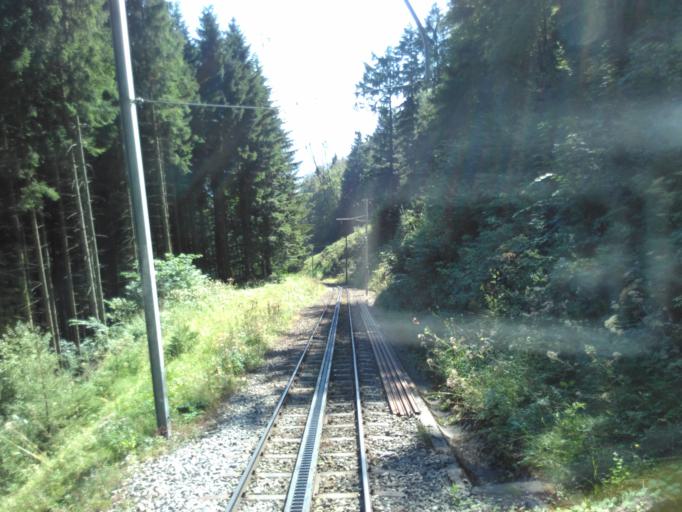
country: CH
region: Schwyz
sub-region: Bezirk Schwyz
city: Goldau
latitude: 47.0388
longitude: 8.5245
